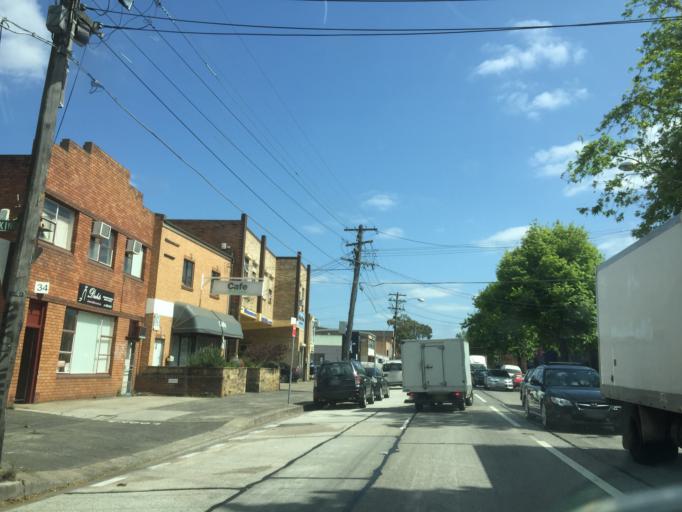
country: AU
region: New South Wales
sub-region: Marrickville
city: Marrickville
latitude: -33.9123
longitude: 151.1656
